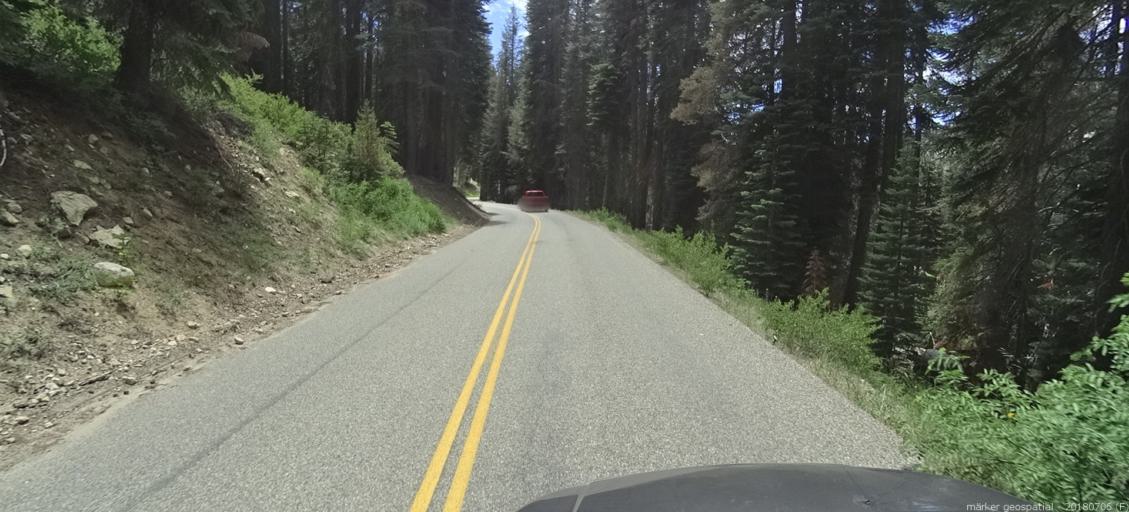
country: US
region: California
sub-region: Madera County
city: Oakhurst
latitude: 37.4366
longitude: -119.4795
